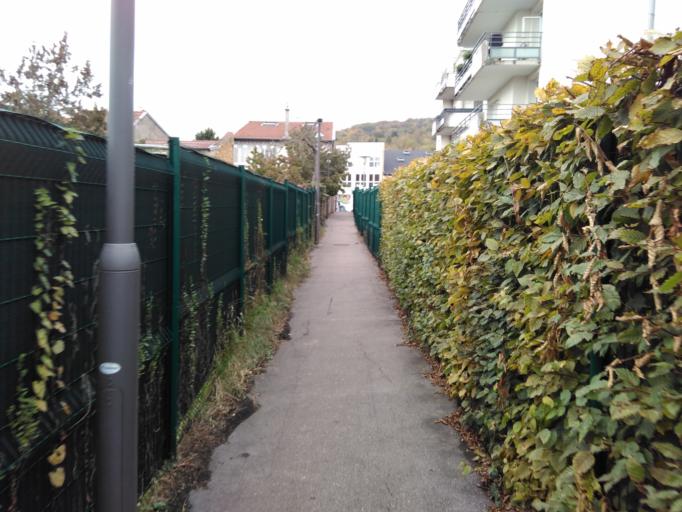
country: FR
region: Lorraine
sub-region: Departement de Meurthe-et-Moselle
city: Essey-les-Nancy
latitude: 48.7045
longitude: 6.2254
